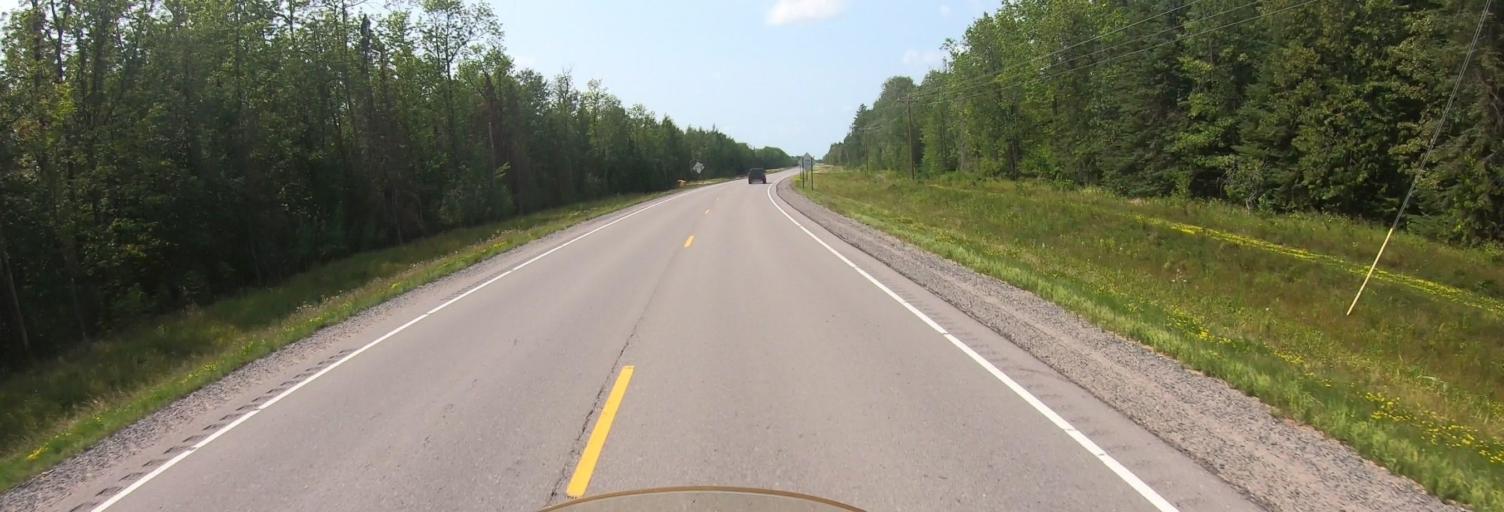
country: US
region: Minnesota
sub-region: Lake of the Woods County
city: Baudette
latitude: 48.6948
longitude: -94.5045
